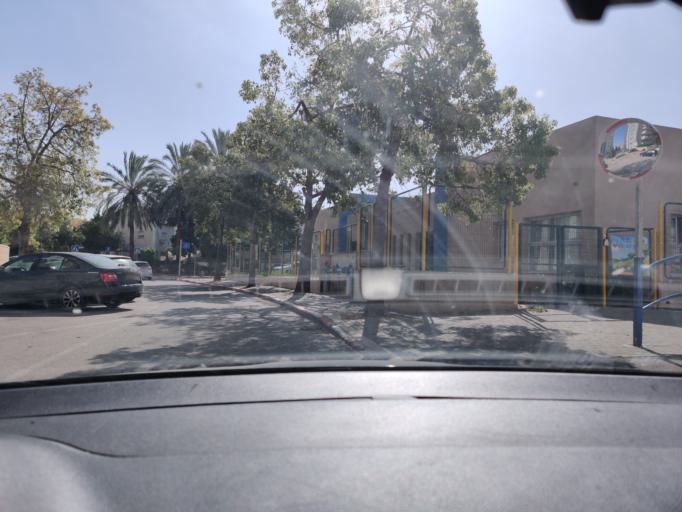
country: IL
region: Haifa
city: Hadera
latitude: 32.4676
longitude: 34.9560
